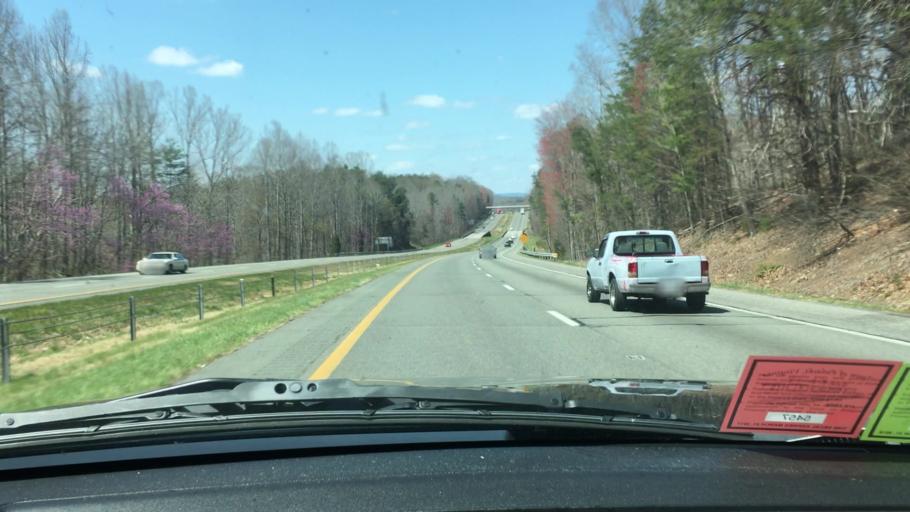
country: US
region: North Carolina
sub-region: Surry County
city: Pilot Mountain
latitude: 36.3811
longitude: -80.4888
